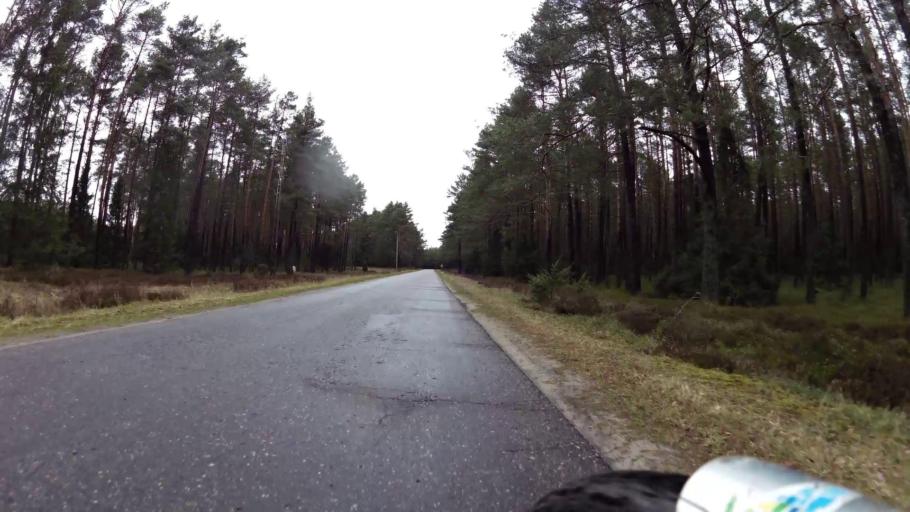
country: PL
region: Pomeranian Voivodeship
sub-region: Powiat bytowski
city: Borzytuchom
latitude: 54.2611
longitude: 17.3664
